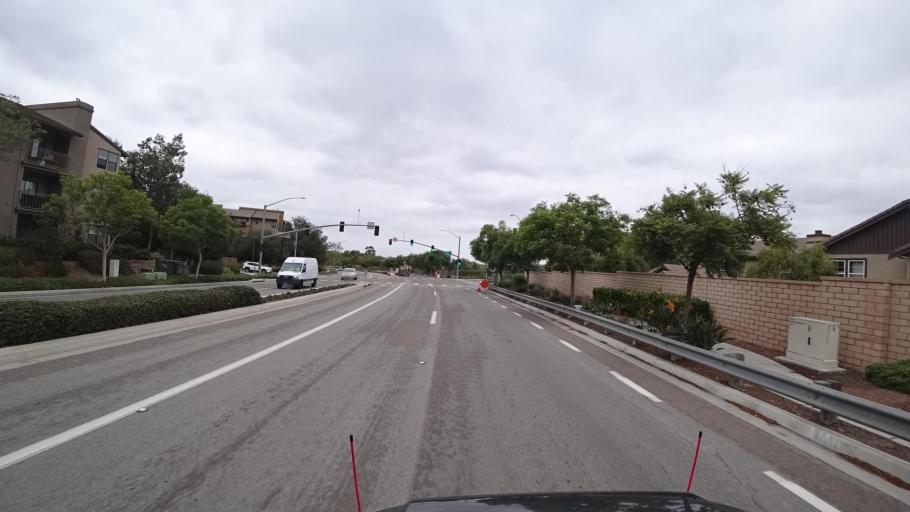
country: US
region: California
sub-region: San Diego County
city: Fairbanks Ranch
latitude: 33.0224
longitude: -117.1147
